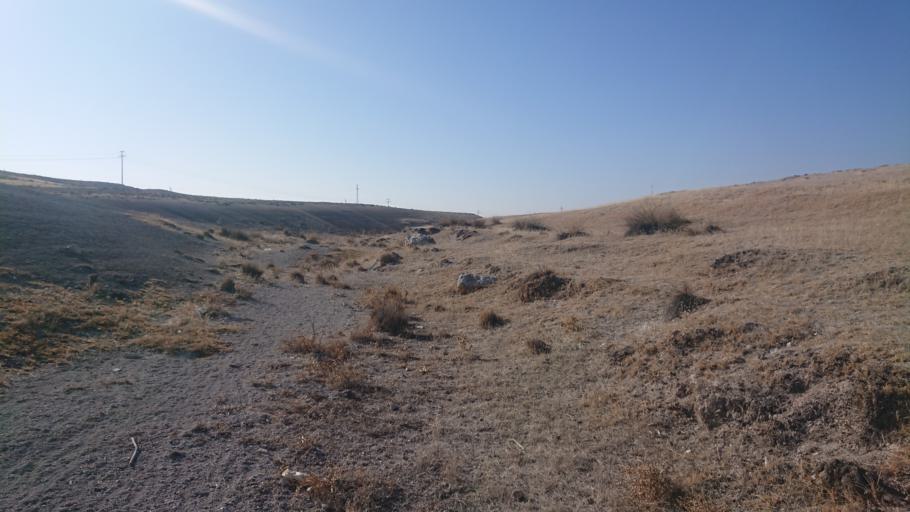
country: TR
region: Aksaray
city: Sultanhani
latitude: 38.2615
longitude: 33.5118
